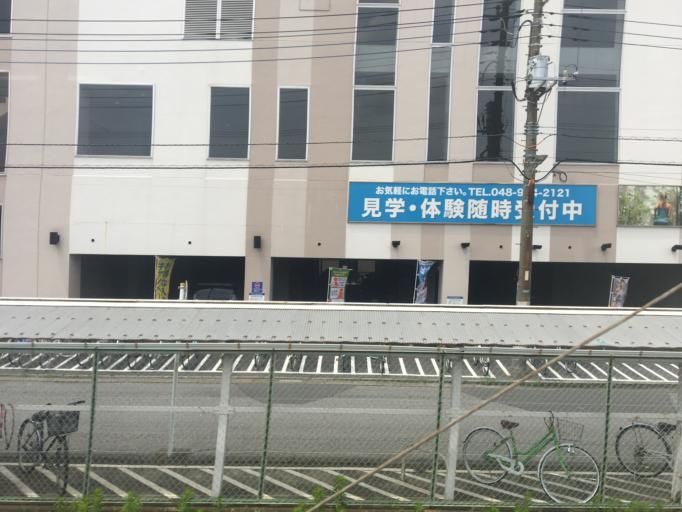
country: JP
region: Saitama
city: Koshigaya
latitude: 35.9342
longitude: 139.7748
